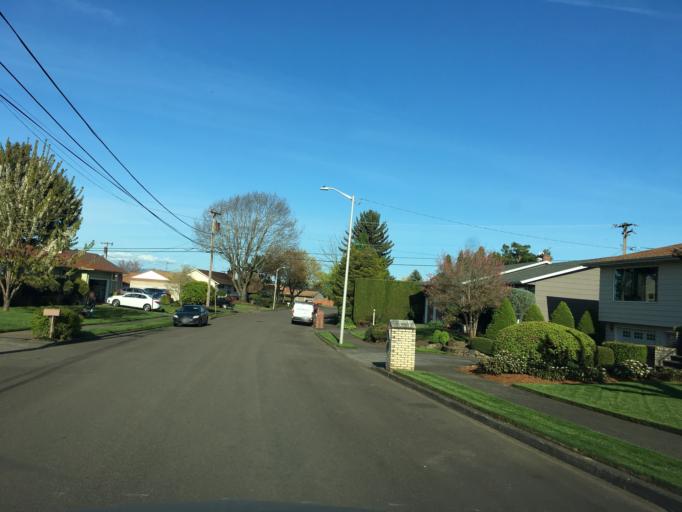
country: US
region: Oregon
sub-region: Multnomah County
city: Lents
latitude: 45.5506
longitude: -122.5276
